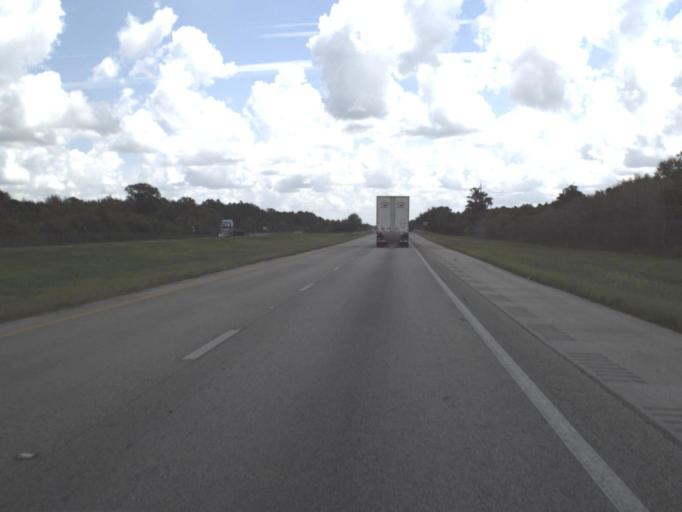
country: US
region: Florida
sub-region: Collier County
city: Orangetree
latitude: 26.1530
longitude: -81.4938
